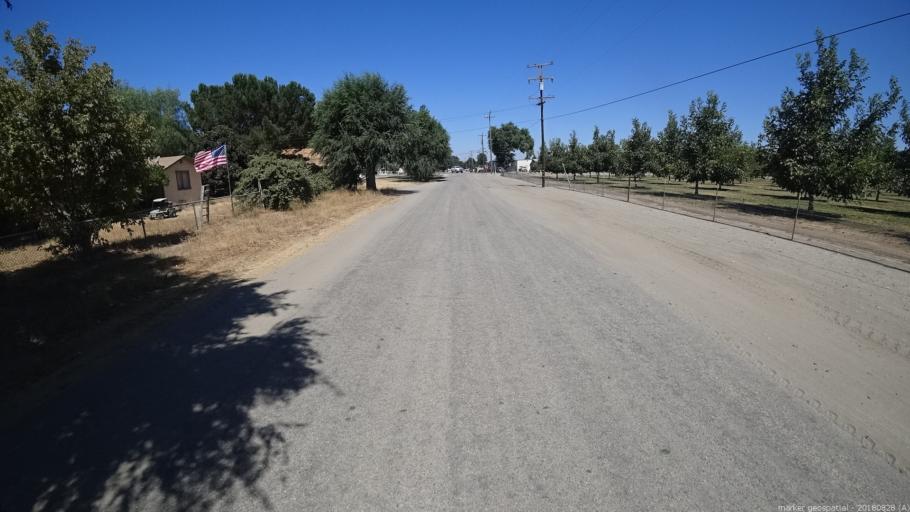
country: US
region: California
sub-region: San Luis Obispo County
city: Lake Nacimiento
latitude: 36.0190
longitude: -120.9013
